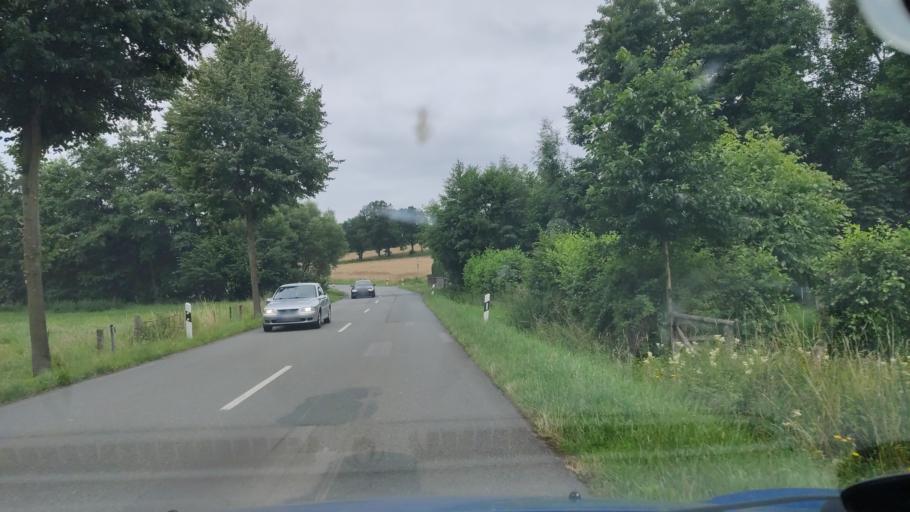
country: DE
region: Lower Saxony
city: Holzminden
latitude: 51.8170
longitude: 9.4752
